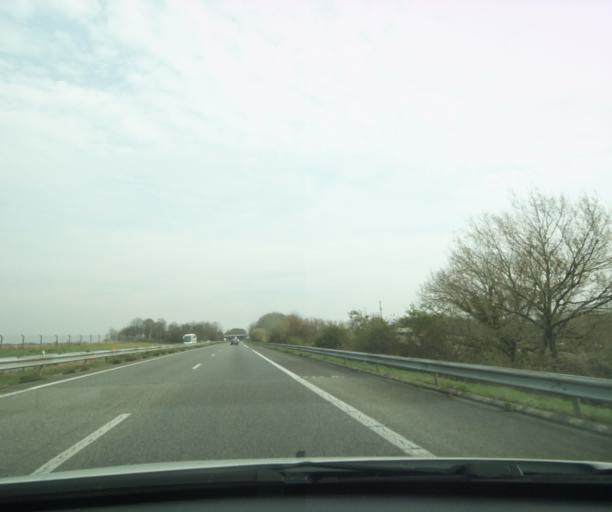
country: FR
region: Aquitaine
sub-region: Departement des Pyrenees-Atlantiques
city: Poey-de-Lescar
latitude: 43.3603
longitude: -0.4665
